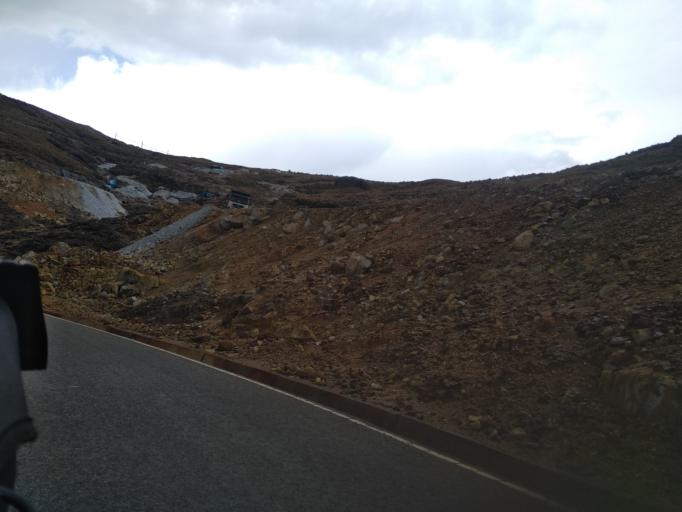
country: PE
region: La Libertad
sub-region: Provincia de Santiago de Chuco
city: Quiruvilca
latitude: -7.9980
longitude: -78.3074
